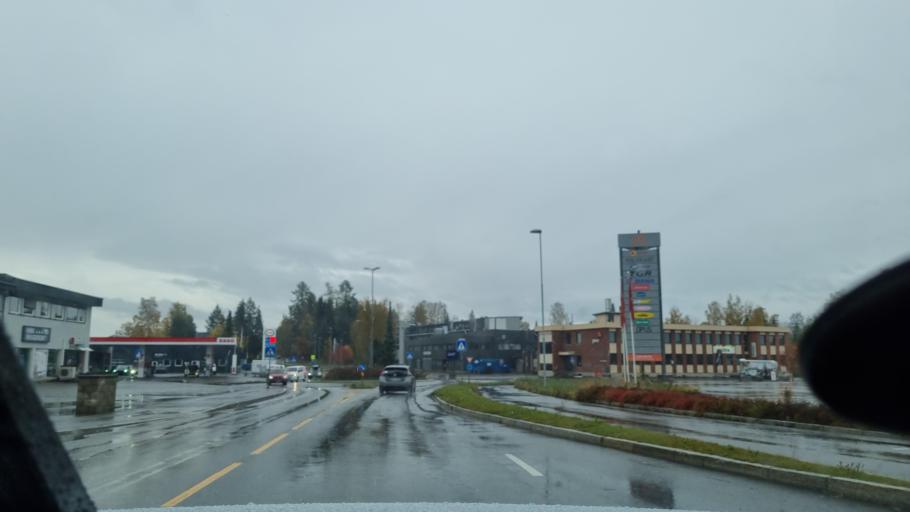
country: NO
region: Hedmark
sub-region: Hamar
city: Hamar
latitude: 60.7989
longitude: 11.0484
